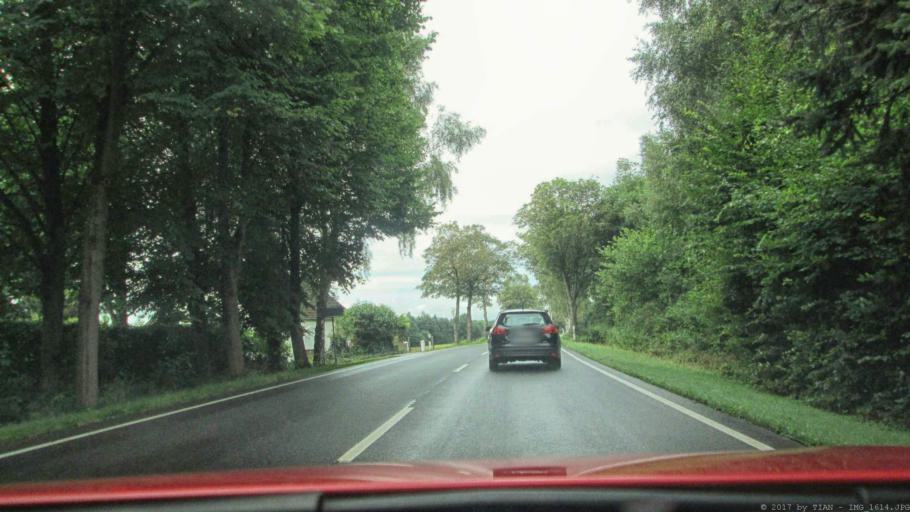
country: DE
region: Lower Saxony
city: Wrestedt
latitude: 52.9224
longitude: 10.6127
